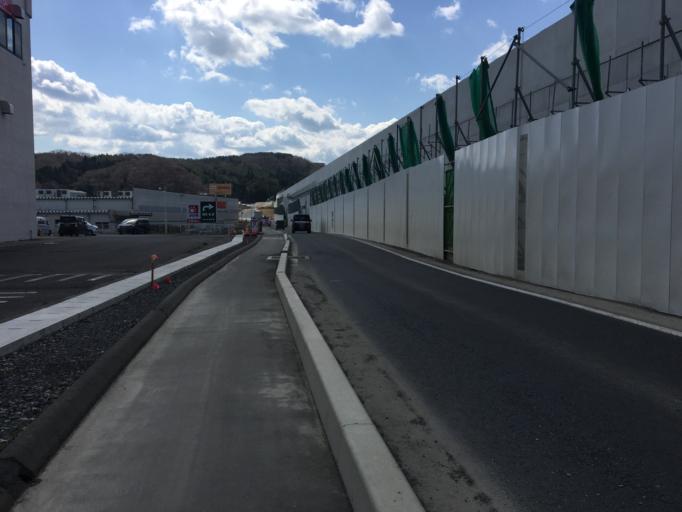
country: JP
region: Aomori
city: Hachinohe
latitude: 40.1909
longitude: 141.7869
